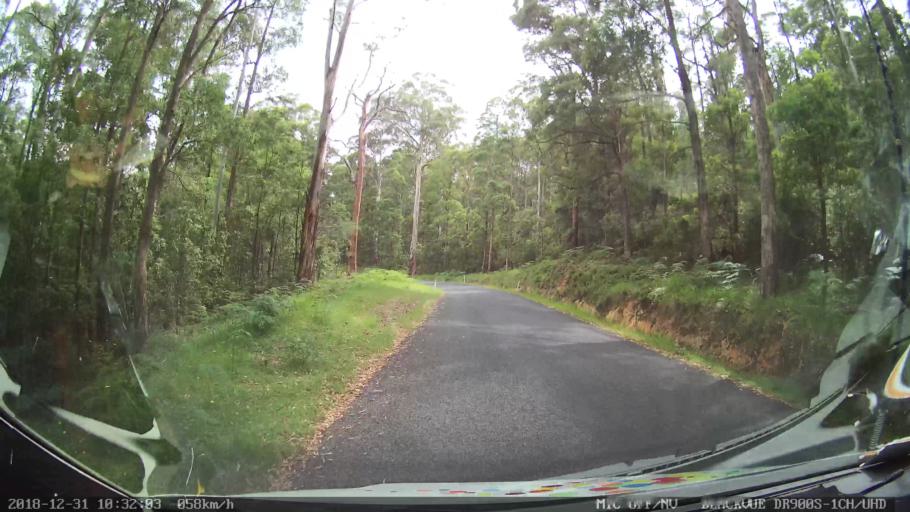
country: AU
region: New South Wales
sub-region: Snowy River
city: Jindabyne
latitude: -36.4534
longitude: 148.1601
